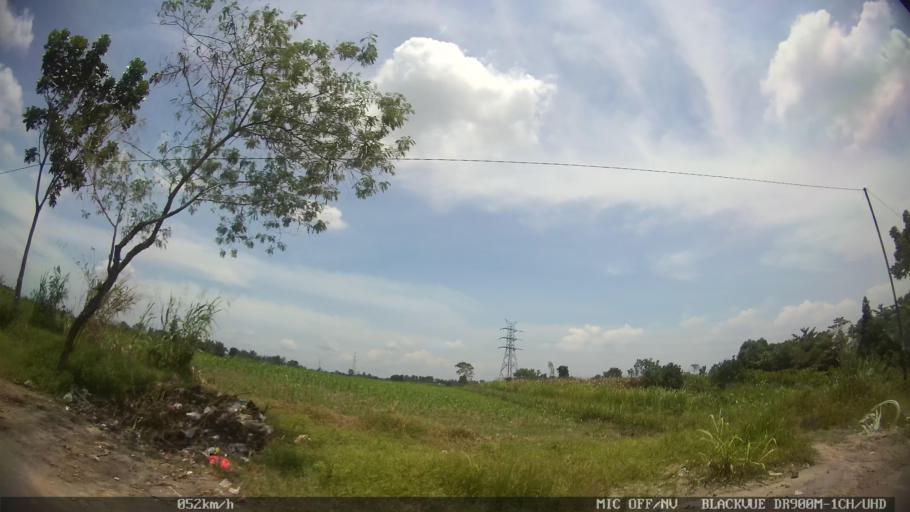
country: ID
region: North Sumatra
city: Binjai
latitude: 3.5913
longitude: 98.5277
